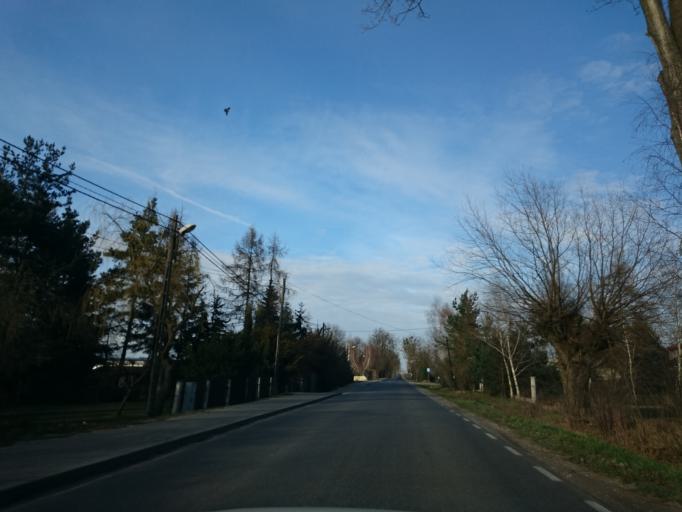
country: PL
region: Kujawsko-Pomorskie
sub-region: Powiat torunski
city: Lubicz Gorny
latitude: 53.0360
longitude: 18.7813
